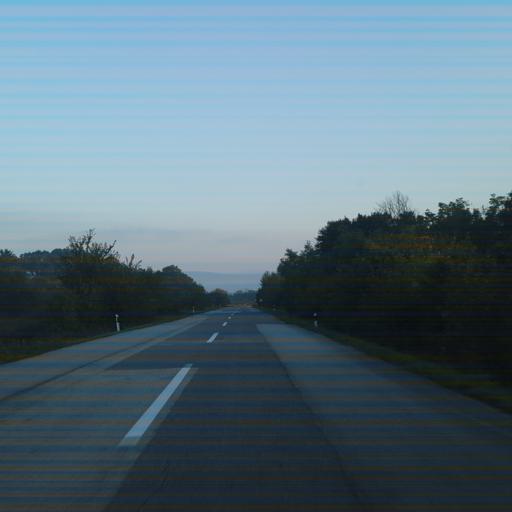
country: RS
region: Central Serbia
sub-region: Zajecarski Okrug
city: Zajecar
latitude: 43.9727
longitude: 22.2926
